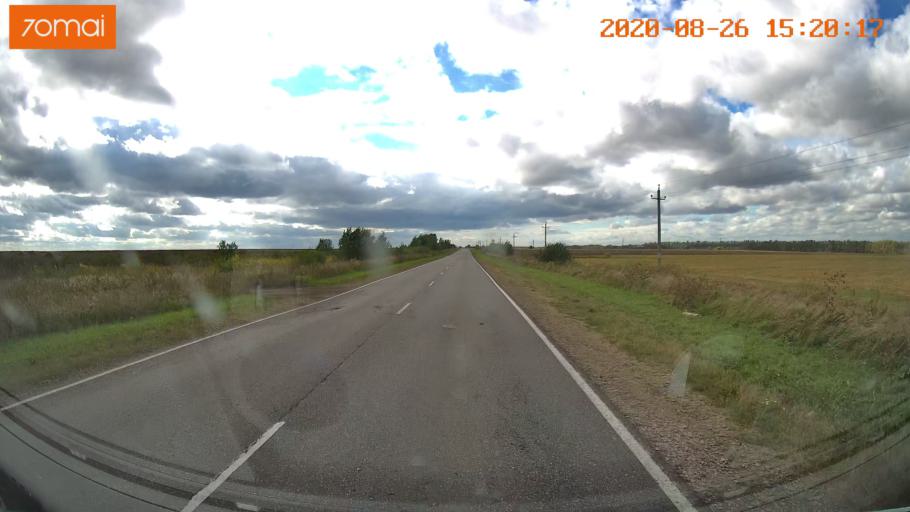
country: RU
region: Tula
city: Severo-Zadonsk
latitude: 54.1425
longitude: 38.5008
